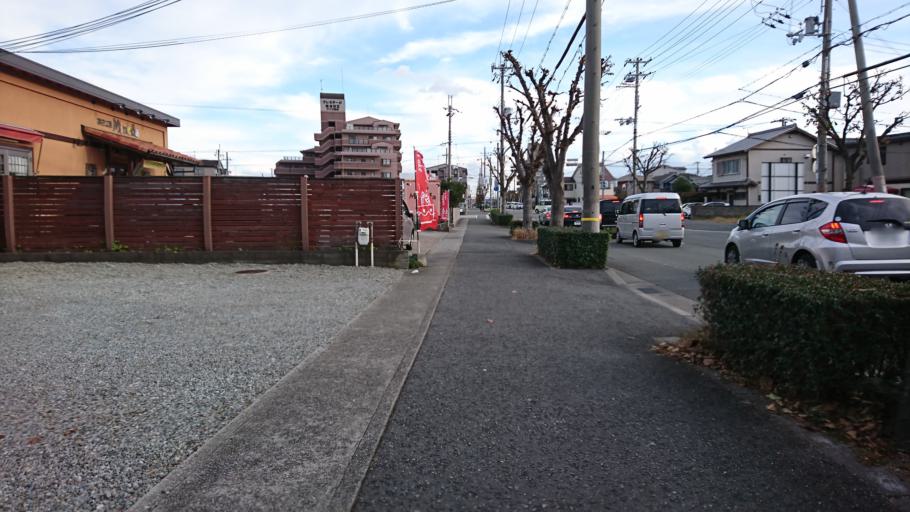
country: JP
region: Hyogo
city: Kakogawacho-honmachi
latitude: 34.7530
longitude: 134.8393
